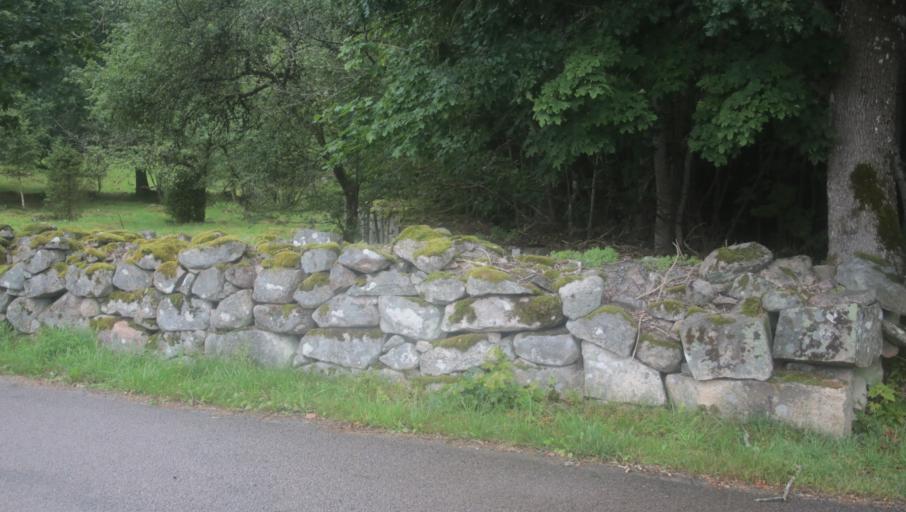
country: SE
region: Blekinge
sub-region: Karlshamns Kommun
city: Svangsta
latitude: 56.3333
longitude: 14.8024
